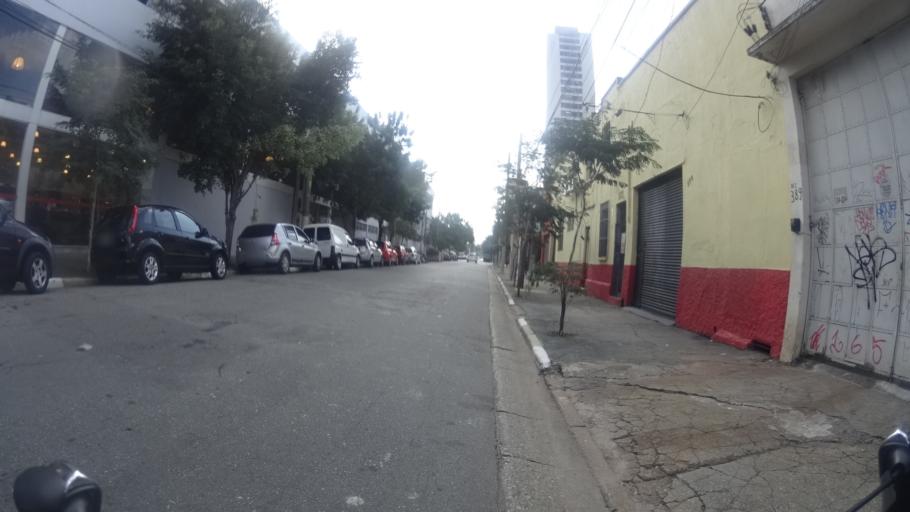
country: BR
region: Sao Paulo
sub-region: Sao Paulo
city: Sao Paulo
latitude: -23.5503
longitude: -46.6076
